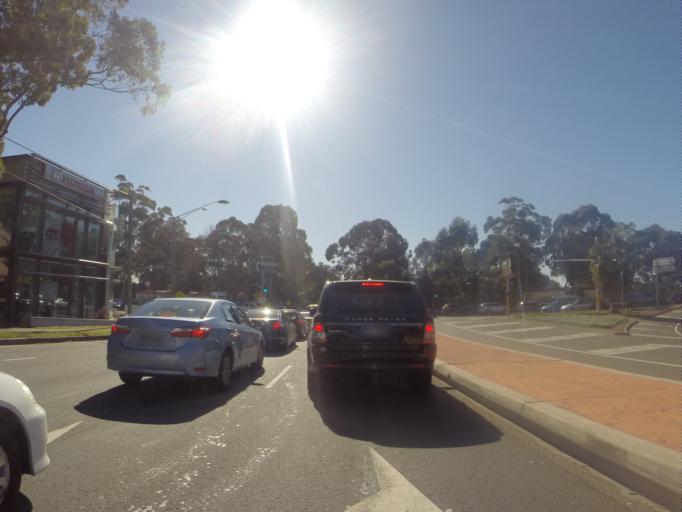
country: AU
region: New South Wales
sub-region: Sutherland Shire
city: Kirrawee
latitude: -34.0320
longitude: 151.0668
